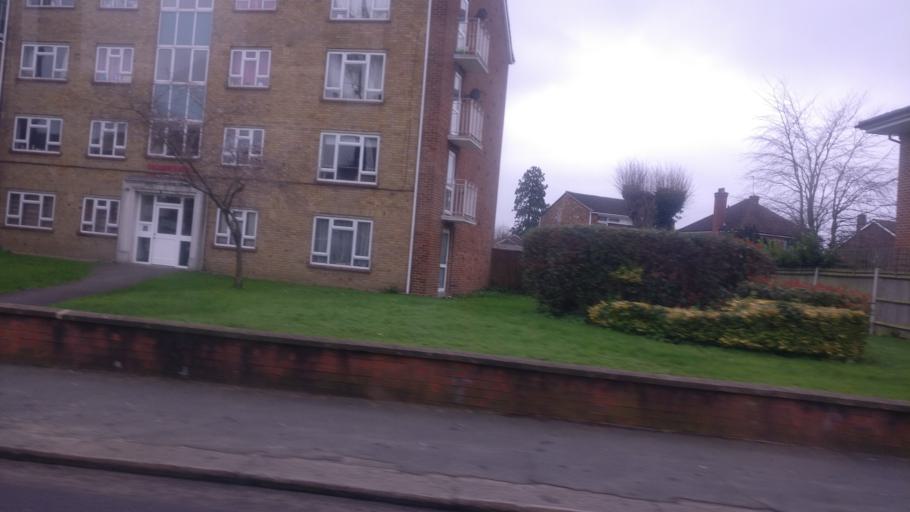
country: GB
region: England
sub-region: Surrey
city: Addlestone
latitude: 51.3732
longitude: -0.4935
